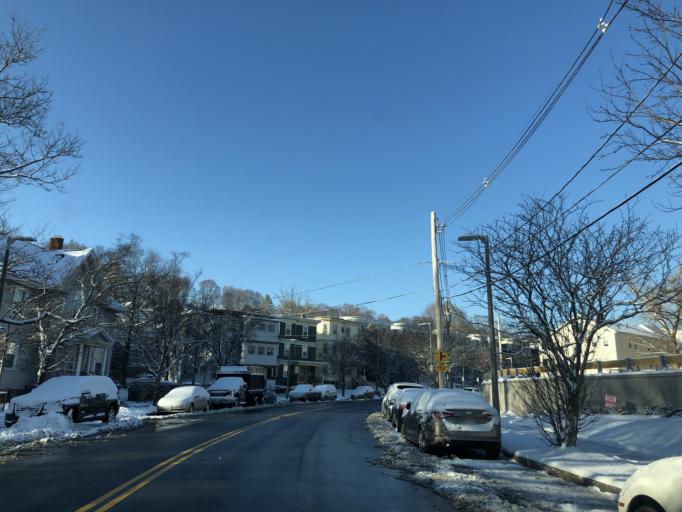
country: US
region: Massachusetts
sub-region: Middlesex County
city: Watertown
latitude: 42.3503
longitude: -71.1692
